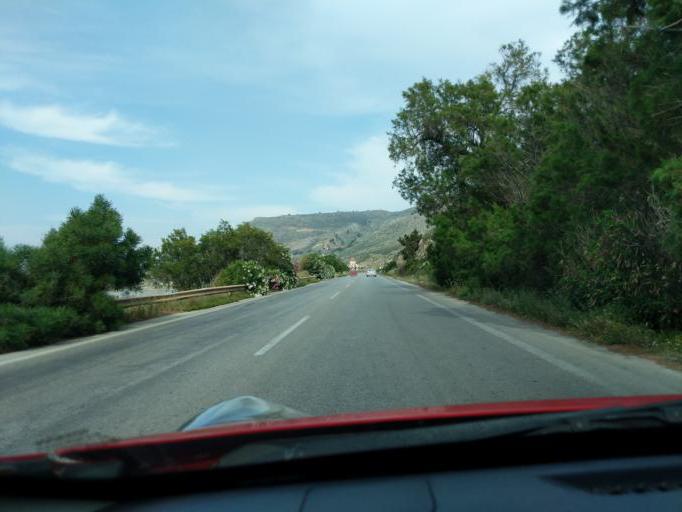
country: GR
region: Crete
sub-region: Nomos Rethymnis
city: Atsipopoulon
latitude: 35.3506
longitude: 24.3528
